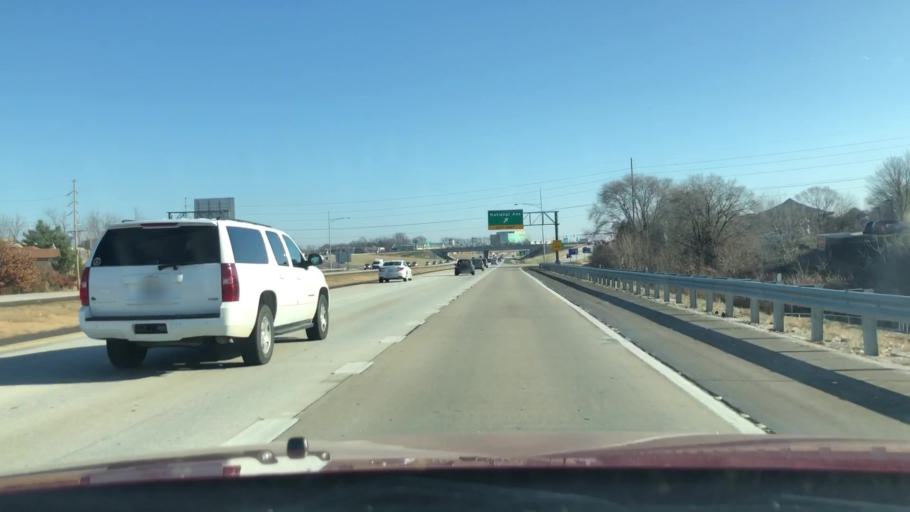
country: US
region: Missouri
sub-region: Greene County
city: Springfield
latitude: 37.1398
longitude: -93.2844
